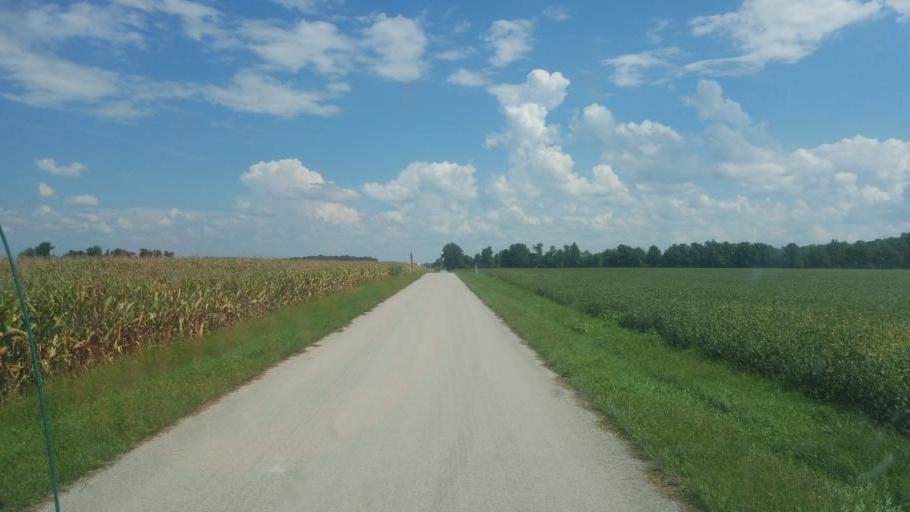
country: US
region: Ohio
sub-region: Hardin County
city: Forest
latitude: 40.8469
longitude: -83.4350
